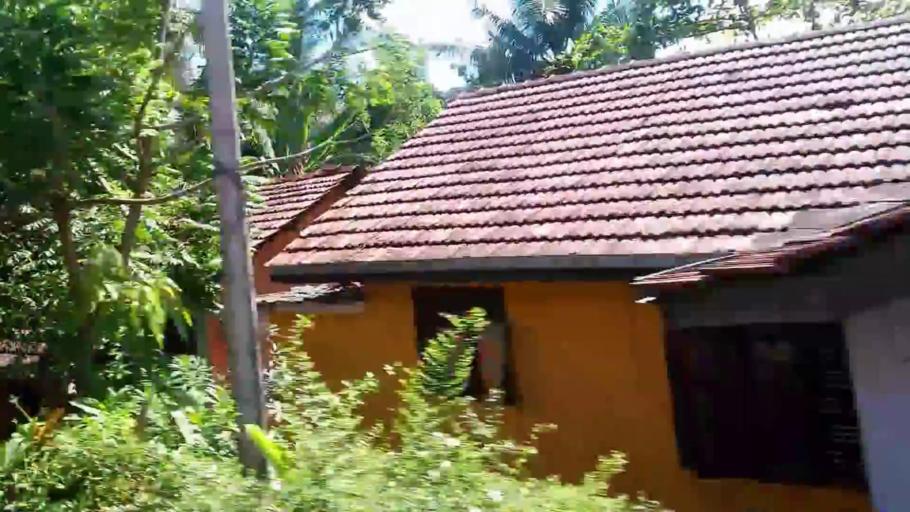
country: LK
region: Southern
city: Hikkaduwa
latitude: 6.1615
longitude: 80.0933
